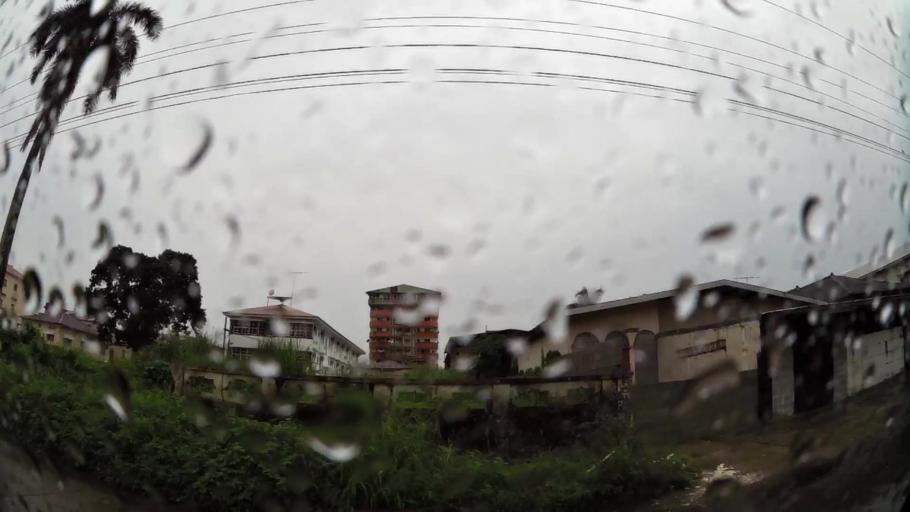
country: PA
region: Colon
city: Colon
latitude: 9.3591
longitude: -79.8969
